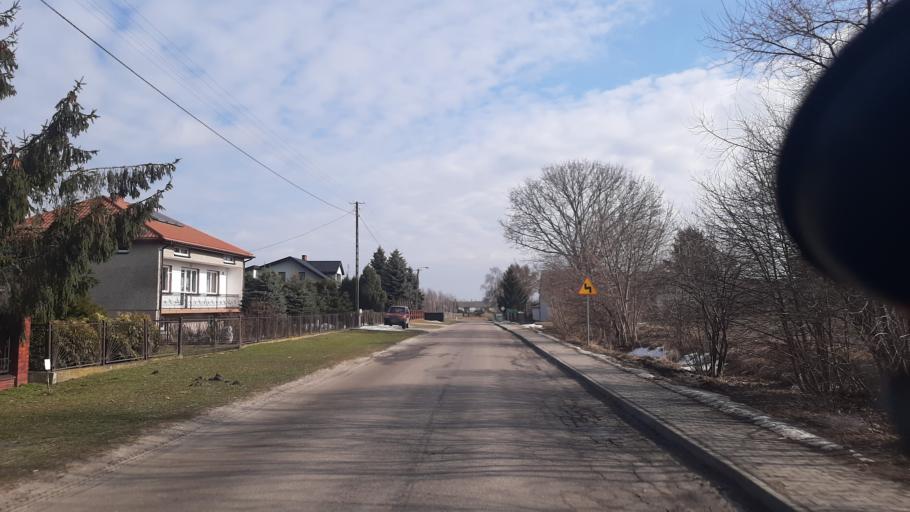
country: PL
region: Lublin Voivodeship
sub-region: Powiat lubartowski
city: Uscimow Stary
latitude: 51.4701
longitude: 22.9527
